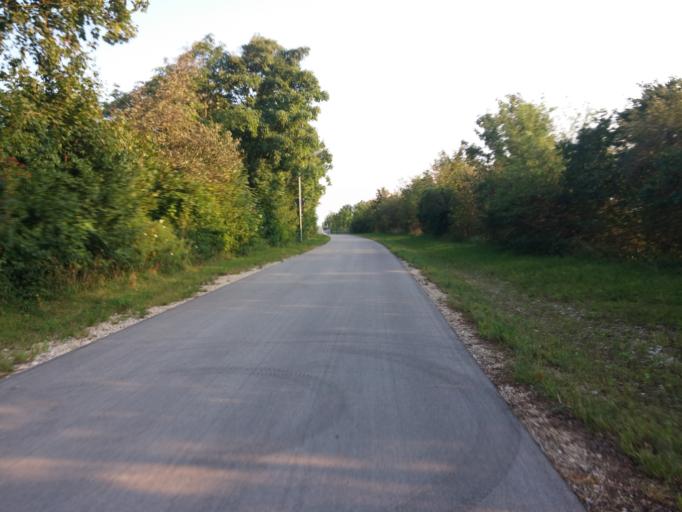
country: DE
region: Bavaria
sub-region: Upper Bavaria
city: Kirchheim bei Muenchen
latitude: 48.1655
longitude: 11.7817
